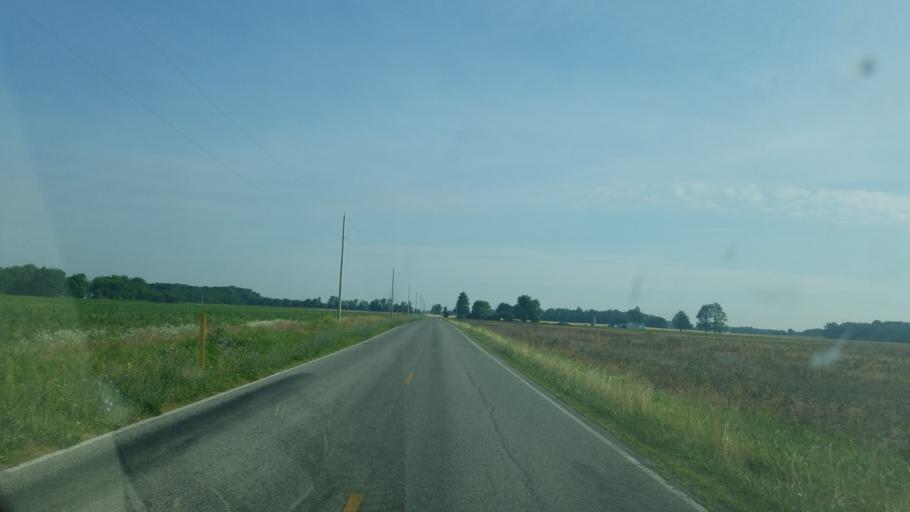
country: US
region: Ohio
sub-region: Hancock County
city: Arlington
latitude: 40.9019
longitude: -83.6985
